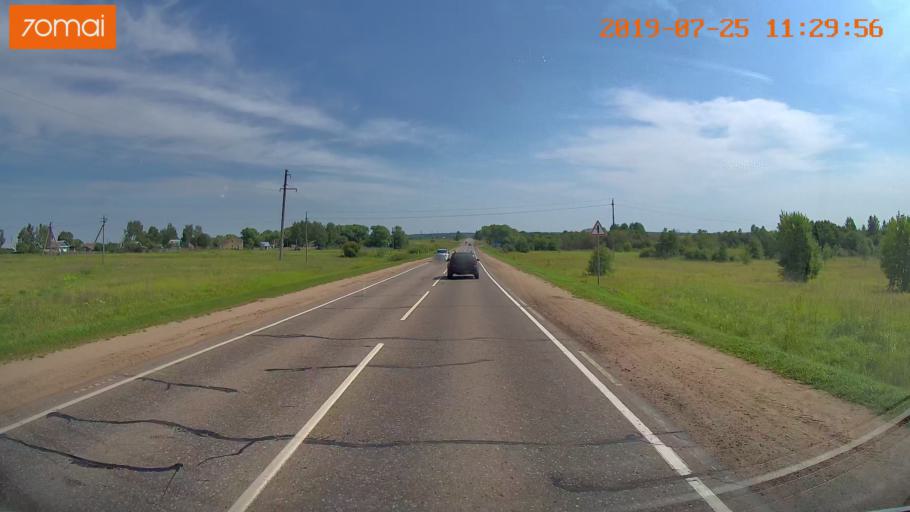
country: RU
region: Ivanovo
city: Privolzhsk
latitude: 57.3866
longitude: 41.3124
